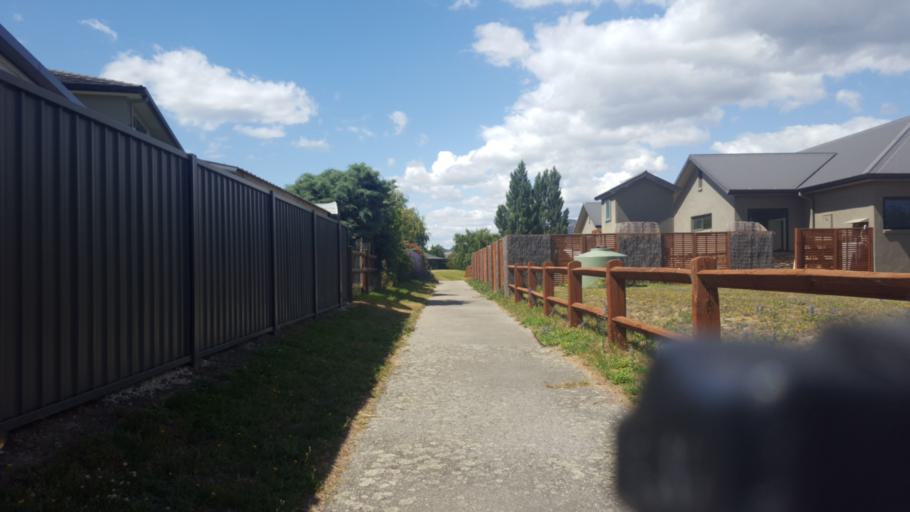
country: NZ
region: Otago
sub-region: Queenstown-Lakes District
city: Wanaka
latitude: -44.9760
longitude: 169.2424
